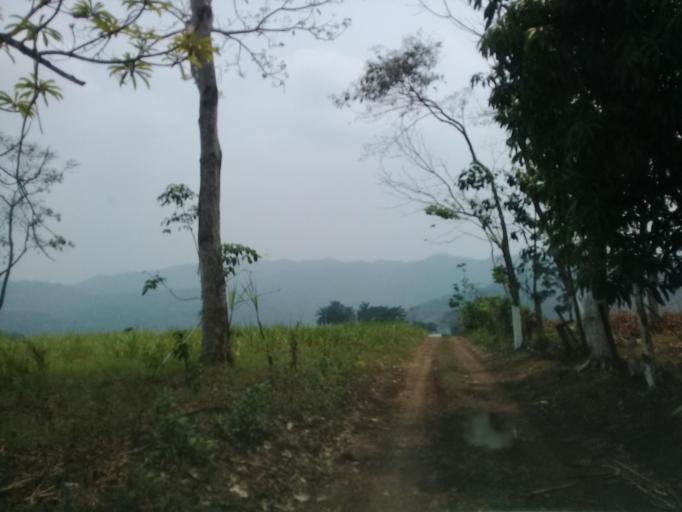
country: MX
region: Veracruz
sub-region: Tezonapa
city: Laguna Chica (Pueblo Nuevo)
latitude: 18.5130
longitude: -96.7151
